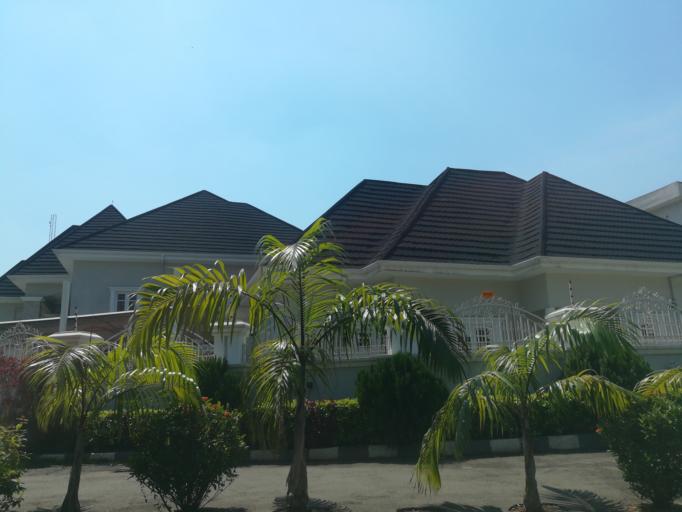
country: NG
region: Abuja Federal Capital Territory
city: Abuja
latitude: 9.0700
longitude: 7.4506
